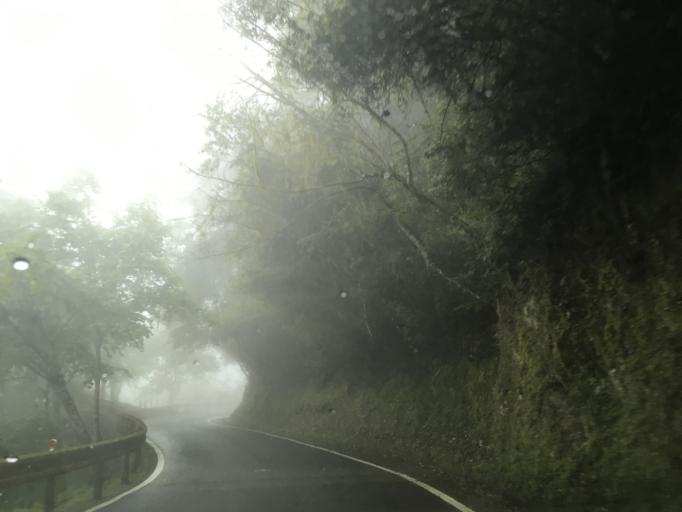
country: TW
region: Taiwan
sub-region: Hualien
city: Hualian
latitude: 24.1913
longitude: 121.4197
